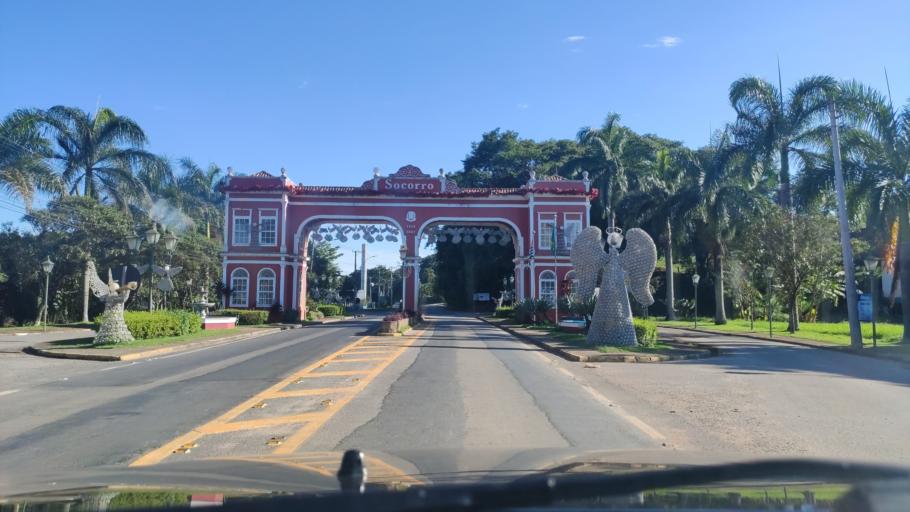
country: BR
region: Sao Paulo
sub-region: Socorro
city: Socorro
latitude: -22.6189
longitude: -46.5328
